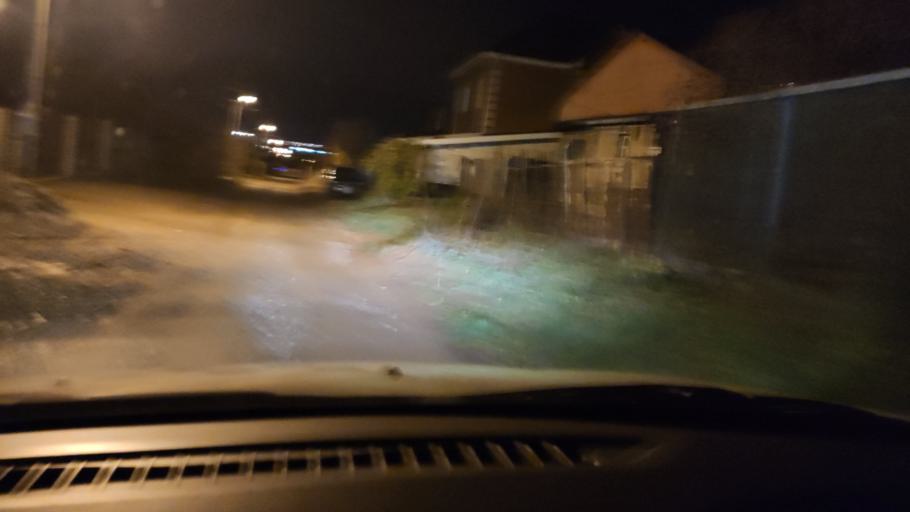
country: RU
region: Perm
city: Kondratovo
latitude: 58.0477
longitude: 56.1177
